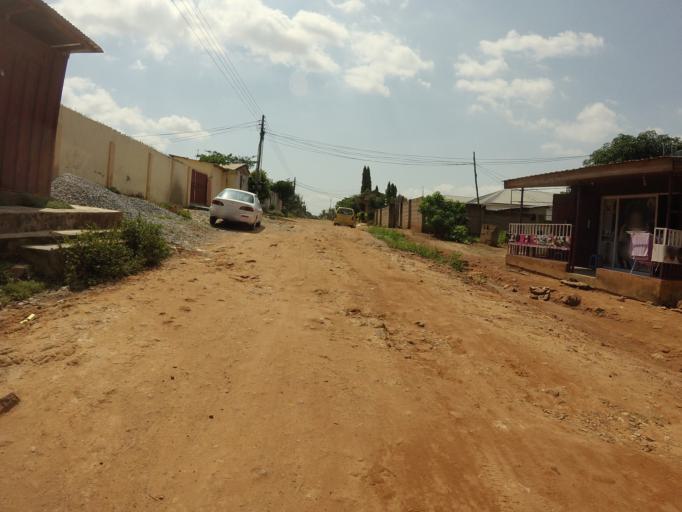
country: GH
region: Greater Accra
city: Gbawe
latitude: 5.6241
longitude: -0.3077
